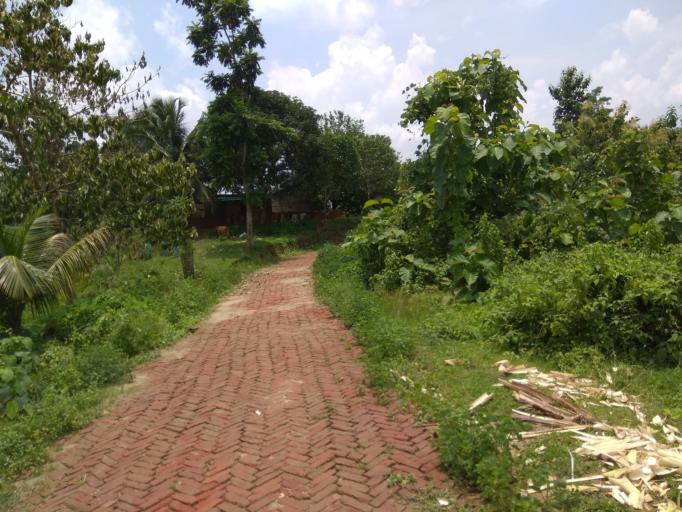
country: BD
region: Chittagong
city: Manikchari
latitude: 22.8851
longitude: 91.9257
